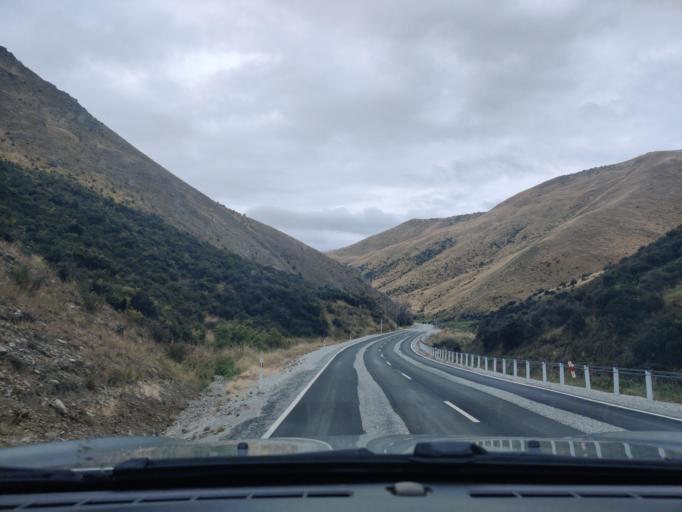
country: NZ
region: Otago
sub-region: Queenstown-Lakes District
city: Wanaka
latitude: -44.6000
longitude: 169.5610
